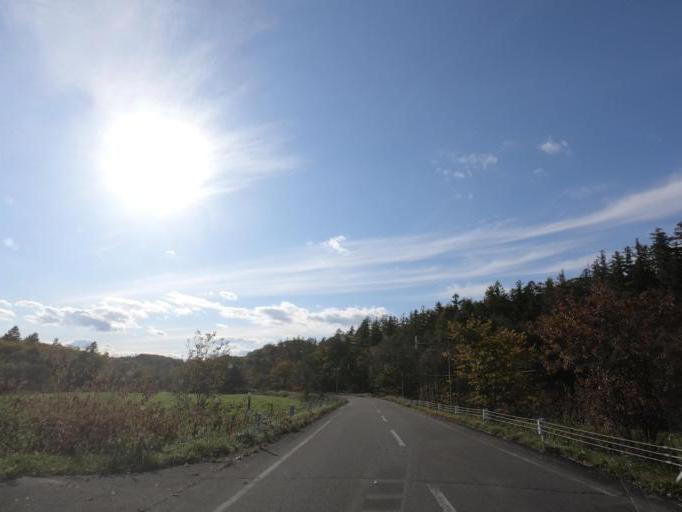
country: JP
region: Hokkaido
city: Obihiro
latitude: 42.6159
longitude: 143.3950
